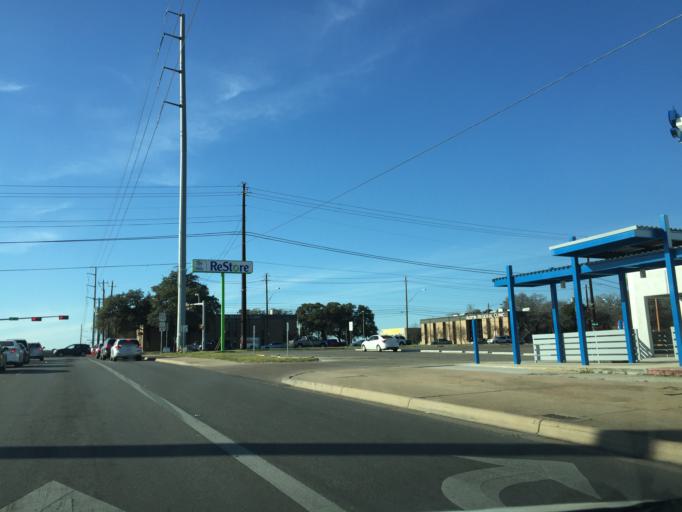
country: US
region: Texas
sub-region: Travis County
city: Austin
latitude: 30.2265
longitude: -97.7684
